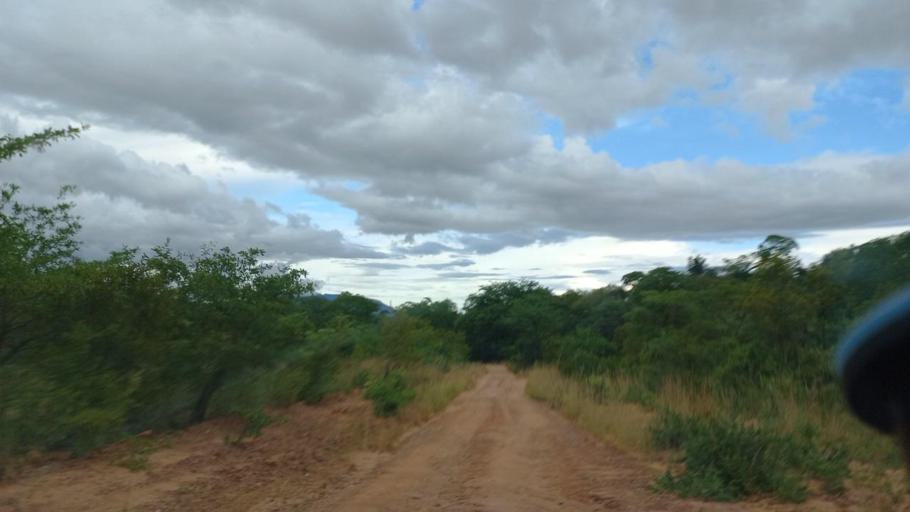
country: ZM
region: Lusaka
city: Luangwa
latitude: -15.5638
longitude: 30.3327
